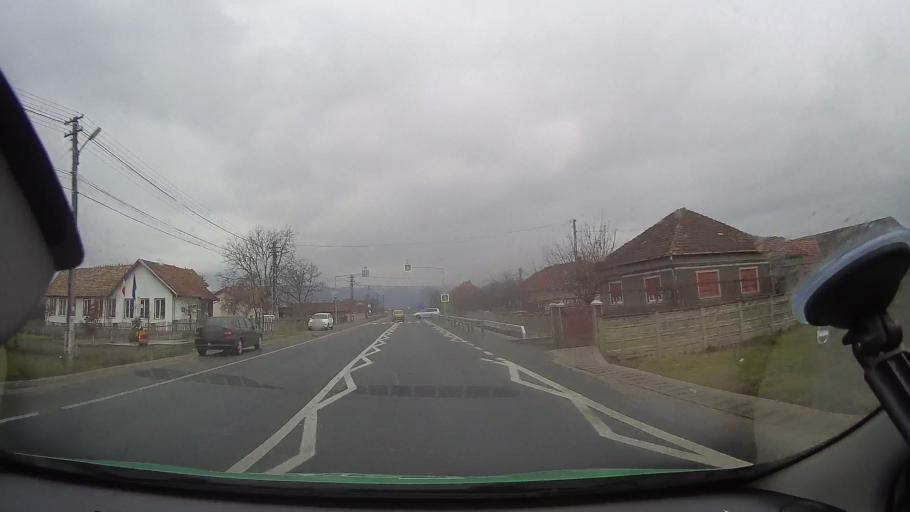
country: RO
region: Hunedoara
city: Vata de Jos
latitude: 46.1911
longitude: 22.6157
